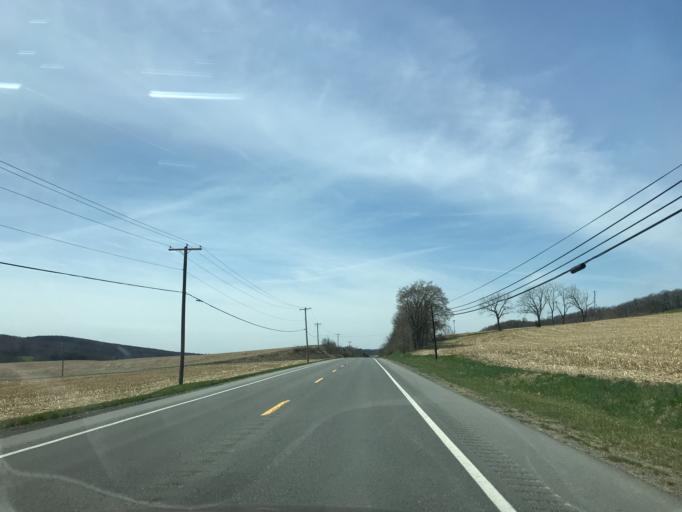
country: US
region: Pennsylvania
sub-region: Snyder County
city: Selinsgrove
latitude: 40.8065
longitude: -76.9341
